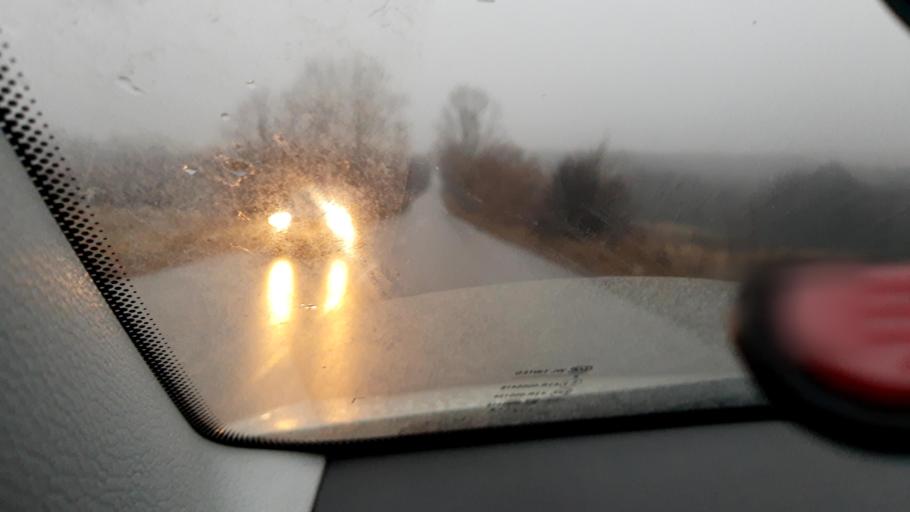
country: RU
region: Bashkortostan
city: Iglino
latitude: 54.8993
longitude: 56.2318
